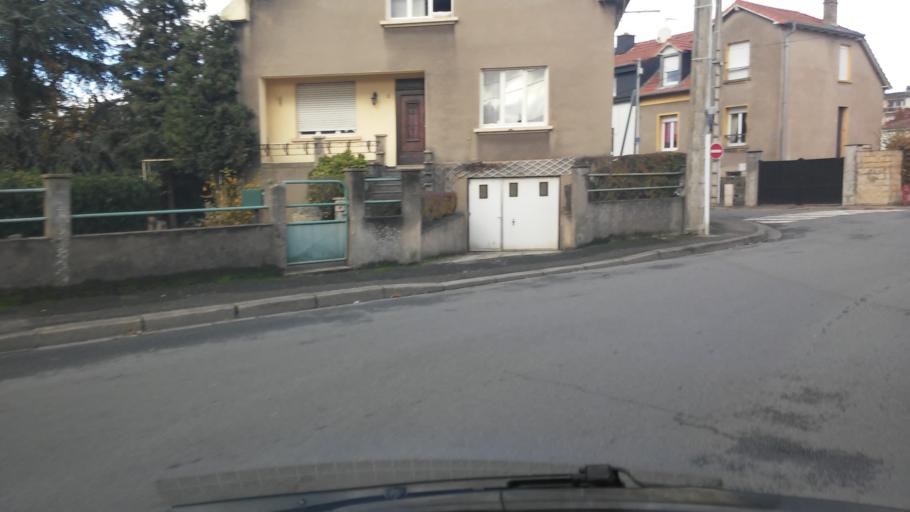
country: FR
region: Lorraine
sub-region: Departement de la Moselle
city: Talange
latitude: 49.2355
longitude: 6.1703
